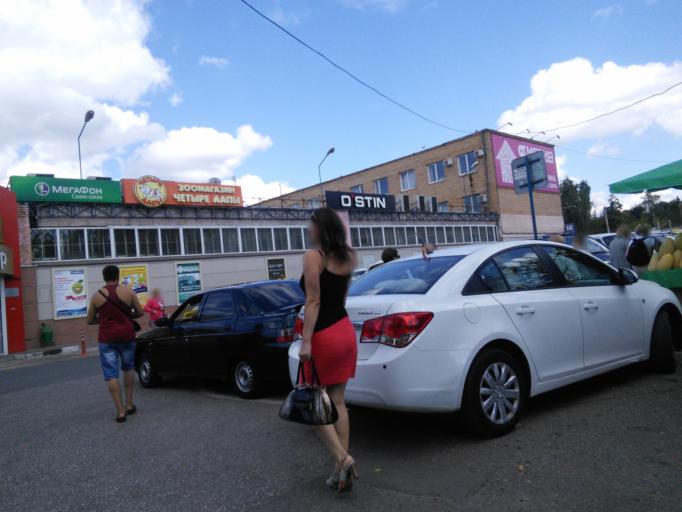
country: RU
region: Moskovskaya
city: Pavlovskiy Posad
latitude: 55.7711
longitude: 38.6521
